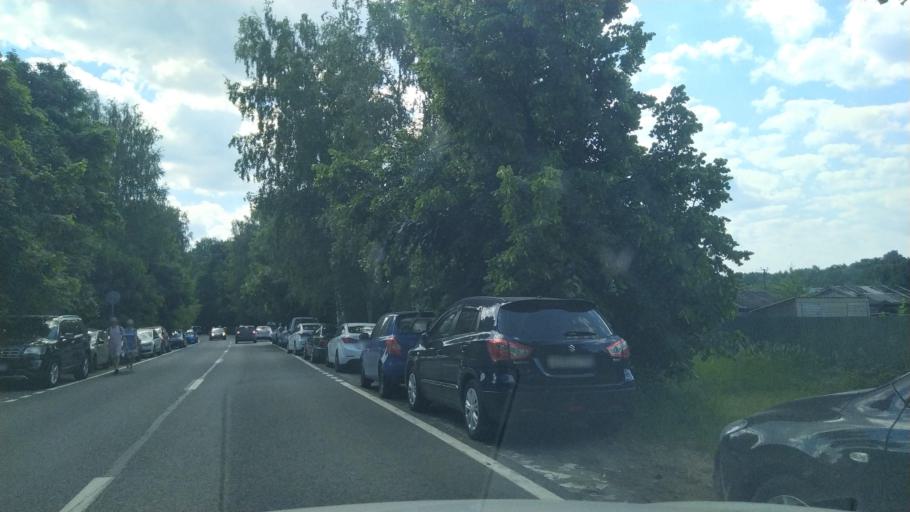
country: RU
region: St.-Petersburg
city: Kronshtadt
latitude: 60.0251
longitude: 29.6828
